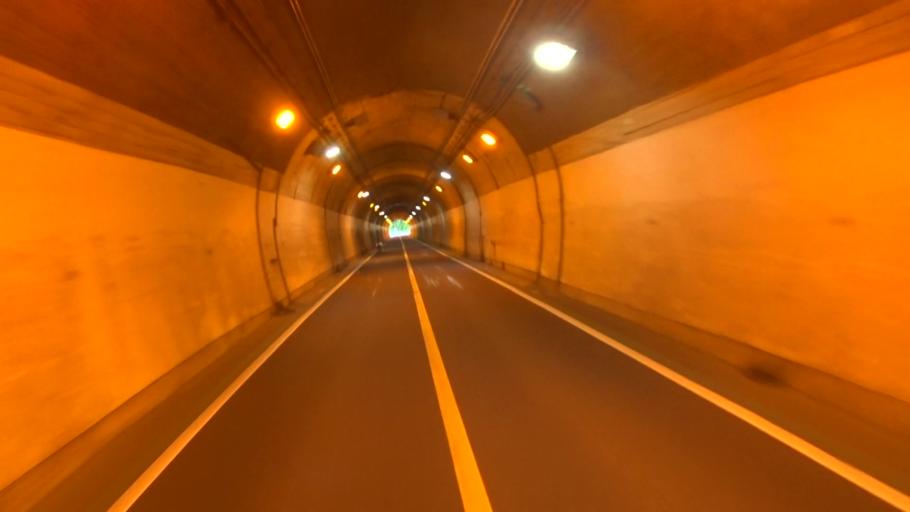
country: JP
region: Kyoto
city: Miyazu
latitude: 35.7353
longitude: 135.0934
